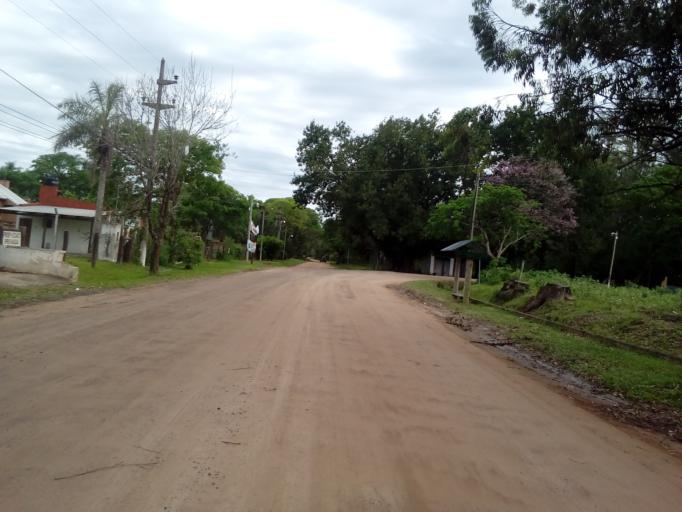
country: AR
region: Corrientes
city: San Luis del Palmar
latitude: -27.4589
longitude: -58.6607
